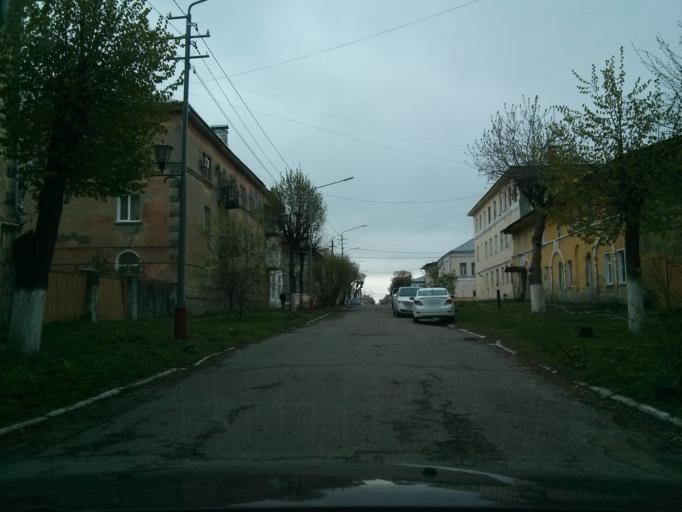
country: RU
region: Vladimir
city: Murom
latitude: 55.5824
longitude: 42.0501
